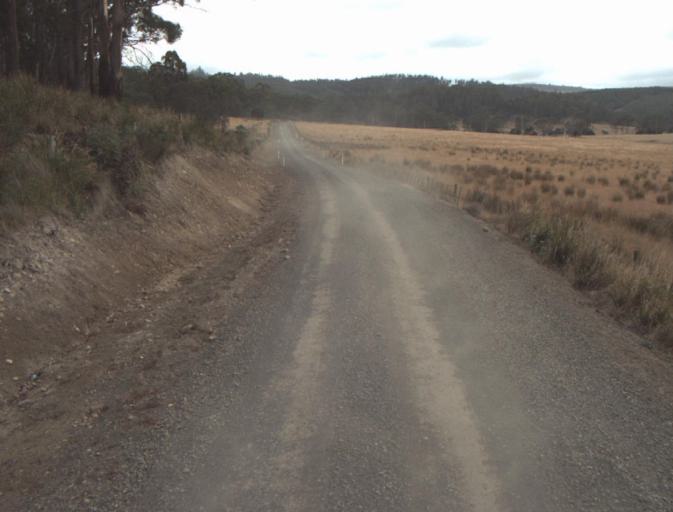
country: AU
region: Tasmania
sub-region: Northern Midlands
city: Evandale
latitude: -41.4731
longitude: 147.4462
